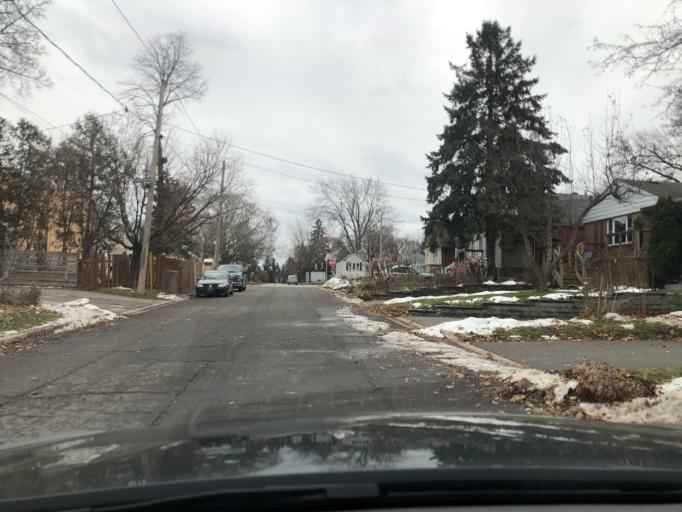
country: CA
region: Ontario
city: Etobicoke
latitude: 43.6976
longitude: -79.5300
